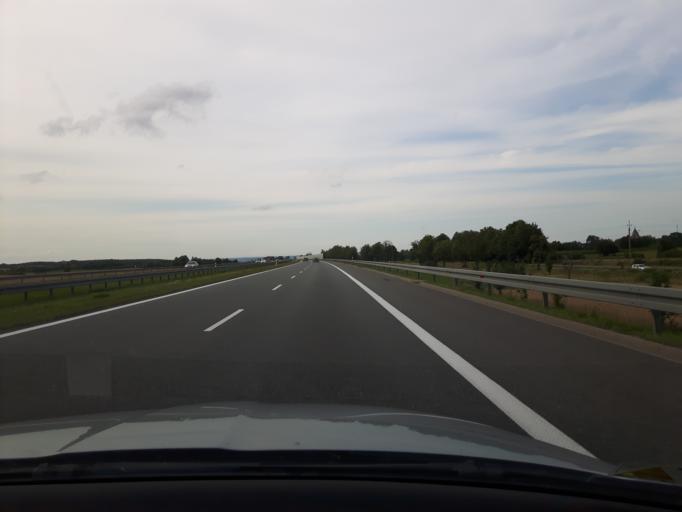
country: PL
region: Warmian-Masurian Voivodeship
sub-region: Powiat elblaski
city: Paslek
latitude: 53.9892
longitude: 19.6946
